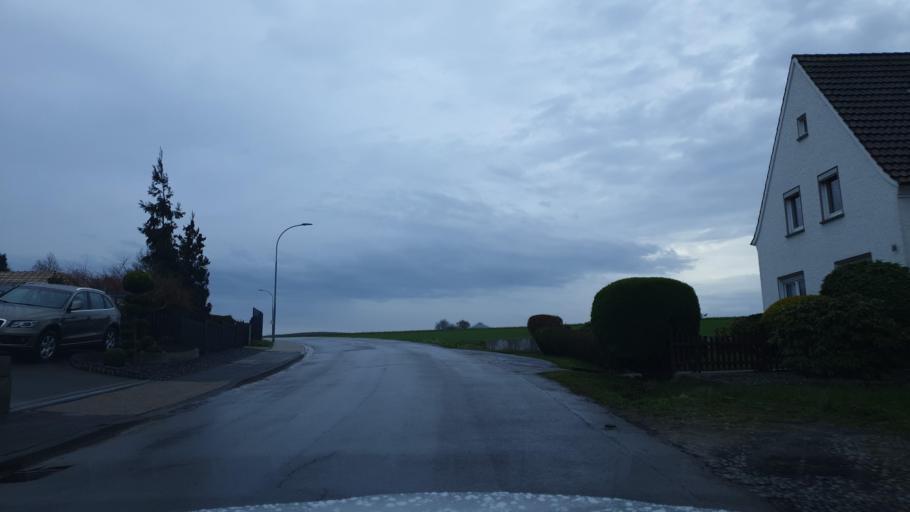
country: DE
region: North Rhine-Westphalia
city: Bad Oeynhausen
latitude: 52.2062
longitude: 8.8293
